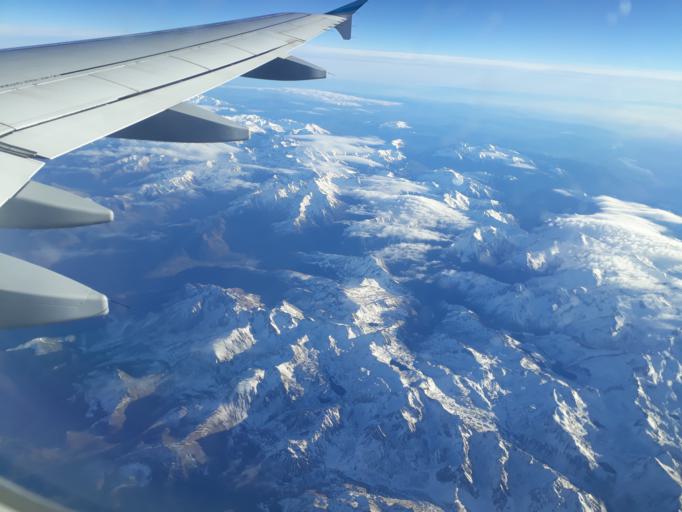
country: FR
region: Midi-Pyrenees
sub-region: Departement des Hautes-Pyrenees
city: Campan
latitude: 42.9903
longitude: 0.1199
